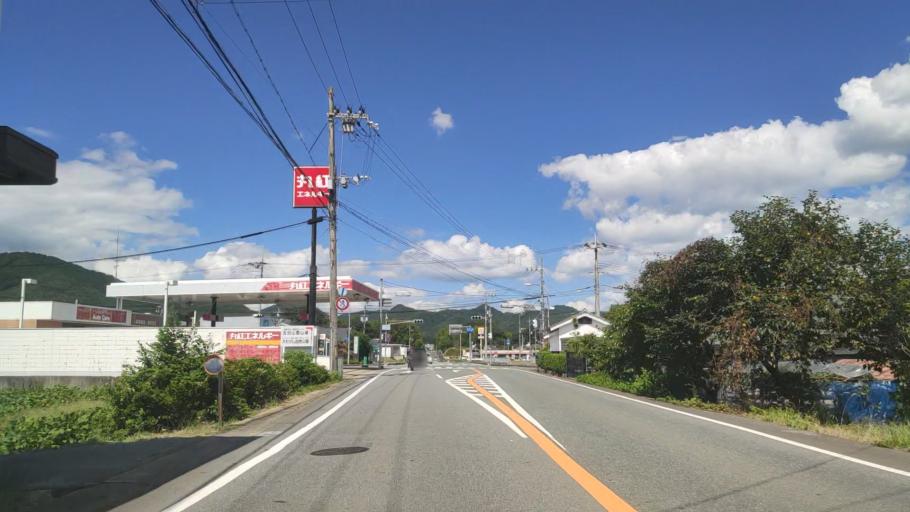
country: JP
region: Kyoto
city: Fukuchiyama
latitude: 35.2267
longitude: 135.1295
